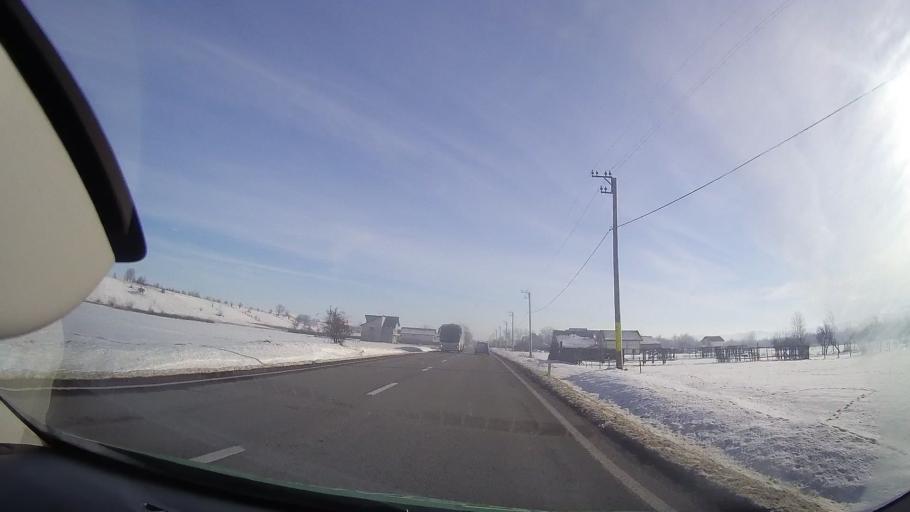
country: RO
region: Neamt
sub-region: Comuna Ghindaoani
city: Ghindaoani
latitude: 47.0846
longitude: 26.3369
